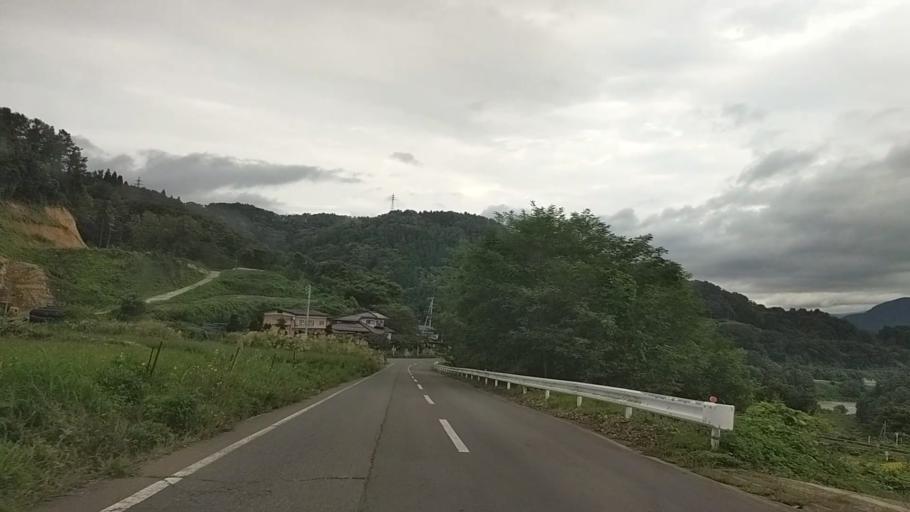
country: JP
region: Nagano
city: Nakano
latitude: 36.7846
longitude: 138.3331
